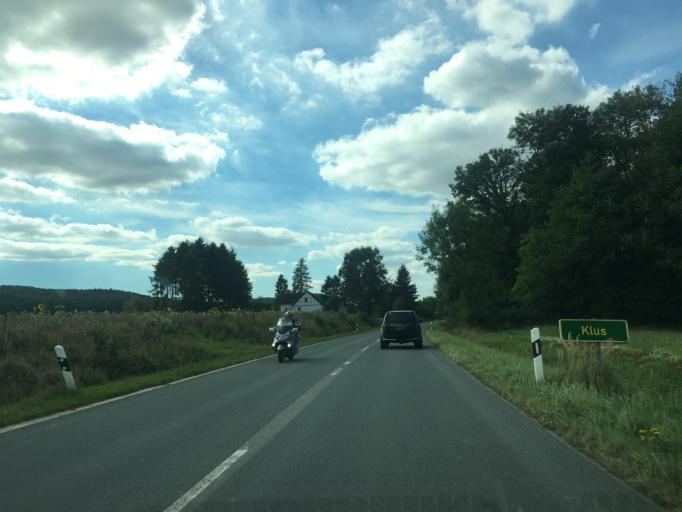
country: DE
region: North Rhine-Westphalia
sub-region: Regierungsbezirk Detmold
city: Barntrup
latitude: 51.9766
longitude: 9.1607
